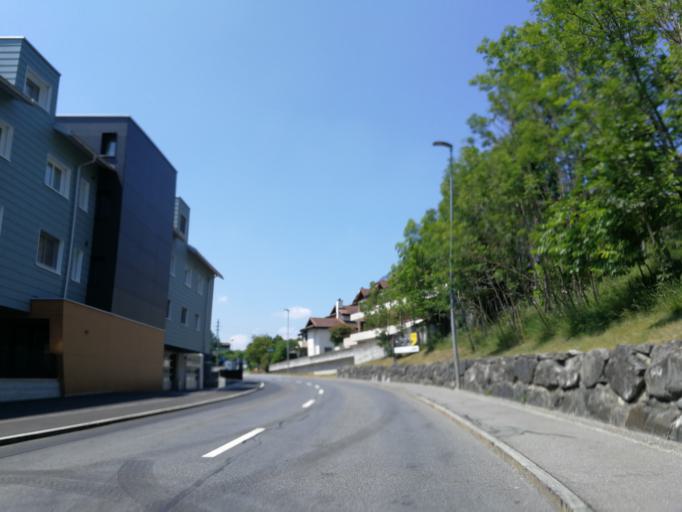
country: CH
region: Zurich
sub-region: Bezirk Horgen
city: Richterswil / Richterswil (Dorfkern)
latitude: 47.1901
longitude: 8.7064
